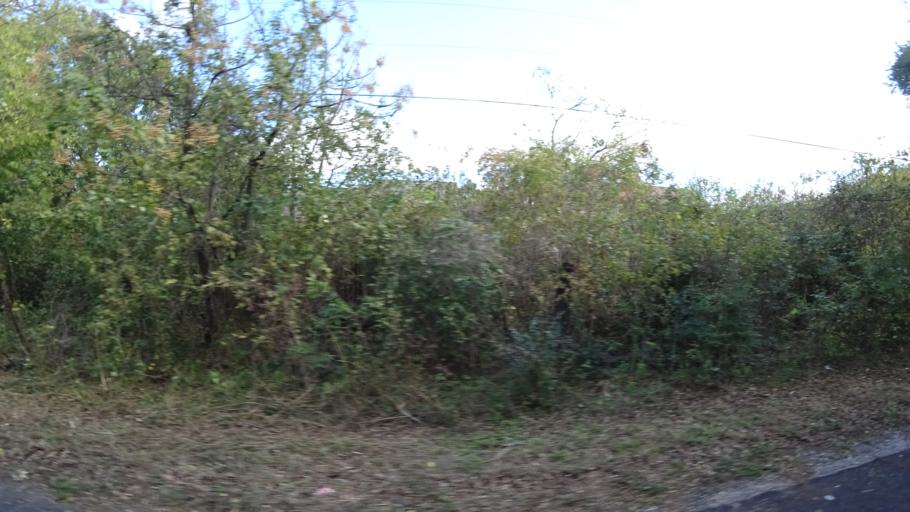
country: US
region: Texas
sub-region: Williamson County
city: Jollyville
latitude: 30.4236
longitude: -97.7298
